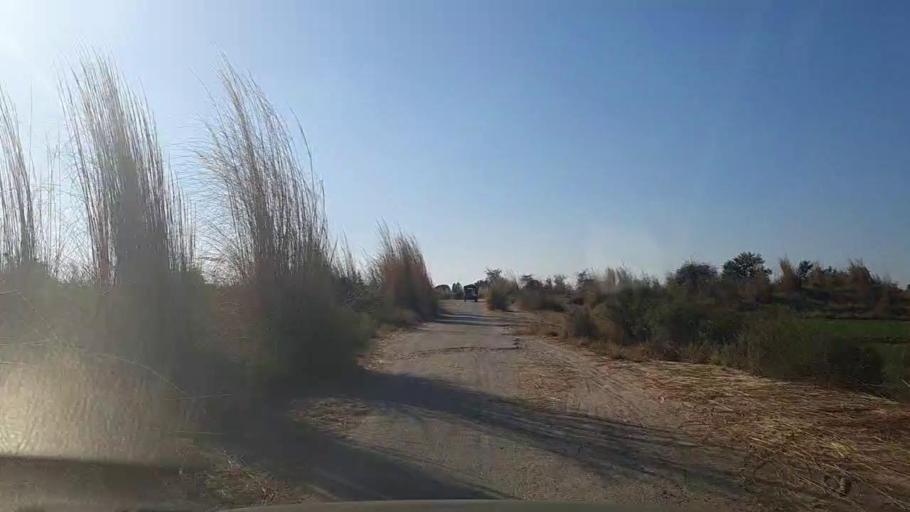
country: PK
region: Sindh
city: Khadro
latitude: 26.2413
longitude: 68.8792
